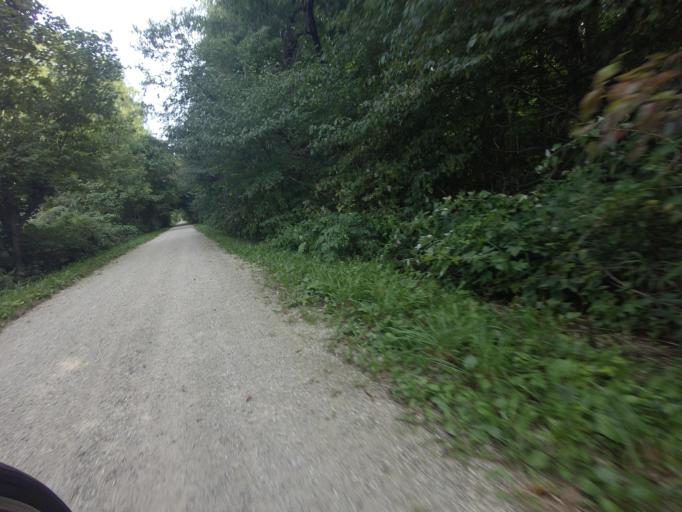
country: CA
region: Ontario
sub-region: Wellington County
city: Guelph
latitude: 43.5710
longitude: -80.3413
